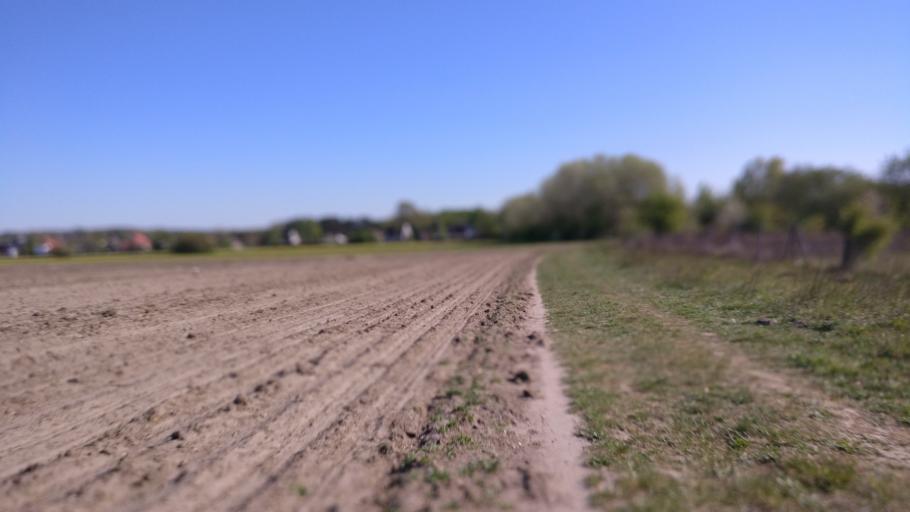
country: DE
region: North Rhine-Westphalia
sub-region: Regierungsbezirk Detmold
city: Lage
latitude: 52.0192
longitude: 8.7591
